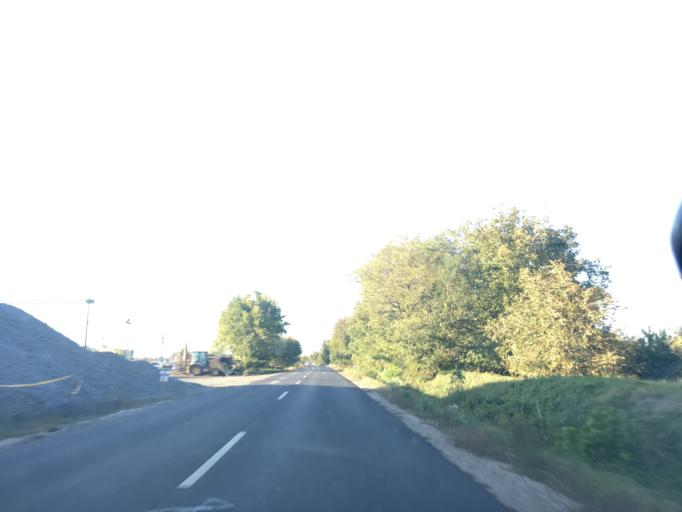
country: HU
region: Pest
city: Szazhalombatta
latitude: 47.3257
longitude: 18.8979
